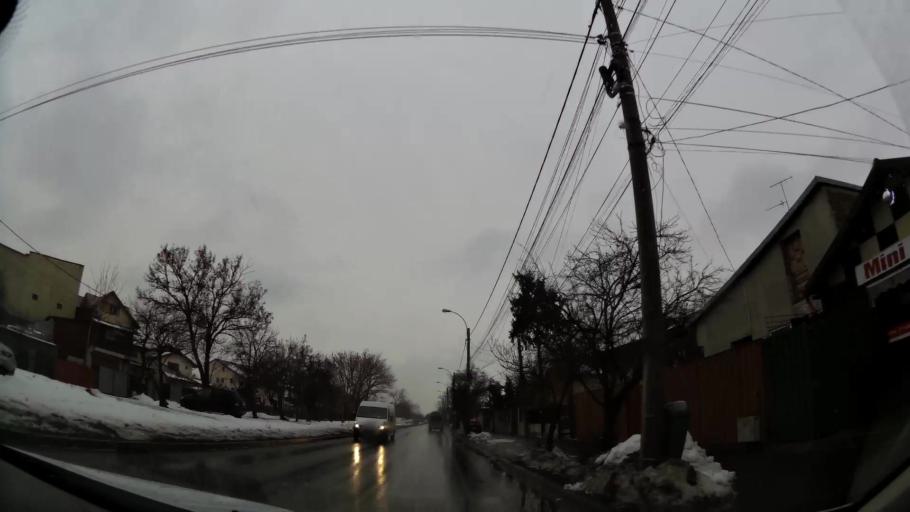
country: RO
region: Ilfov
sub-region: Comuna Chiajna
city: Rosu
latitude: 44.4922
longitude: 26.0283
